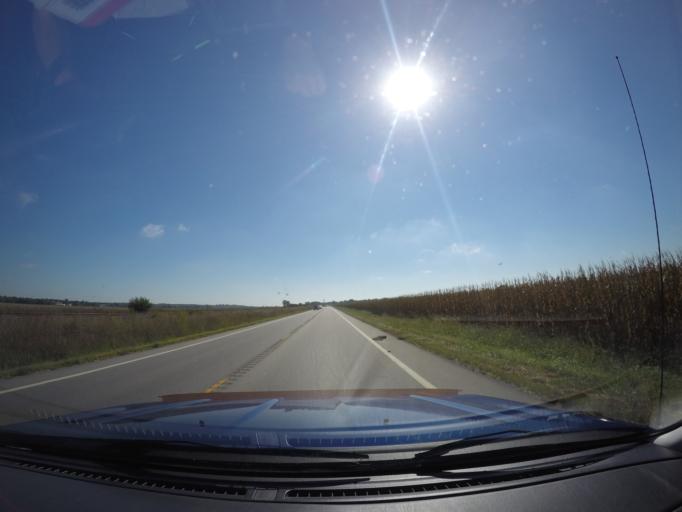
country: US
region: Kansas
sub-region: Shawnee County
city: Silver Lake
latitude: 39.1103
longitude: -95.8801
